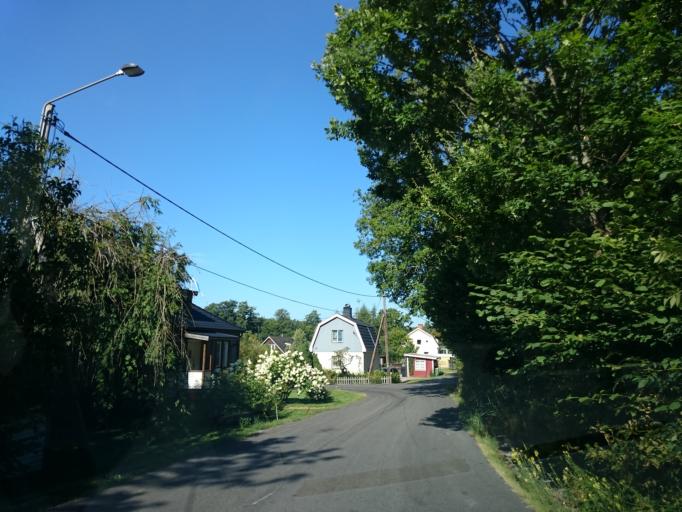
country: SE
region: OEstergoetland
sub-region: Norrkopings Kommun
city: Krokek
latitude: 58.6637
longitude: 16.3897
